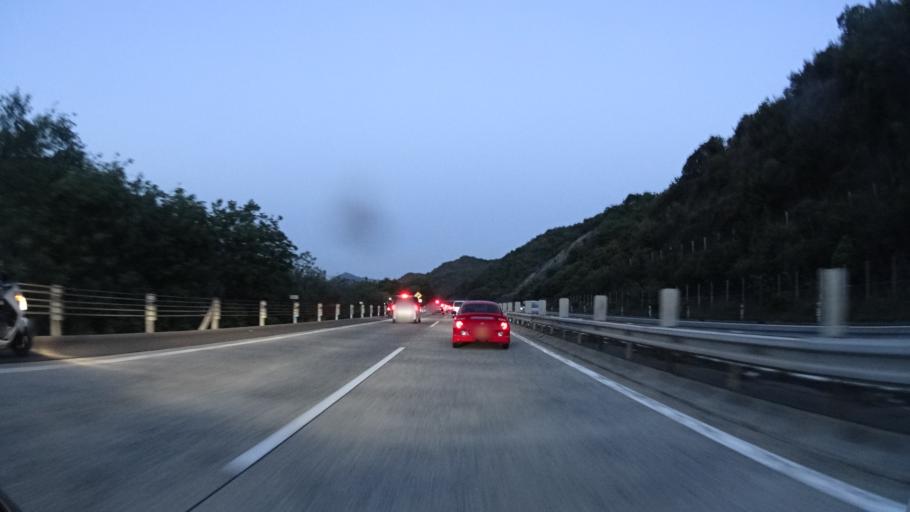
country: JP
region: Hyogo
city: Kariya
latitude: 34.7805
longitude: 134.3209
